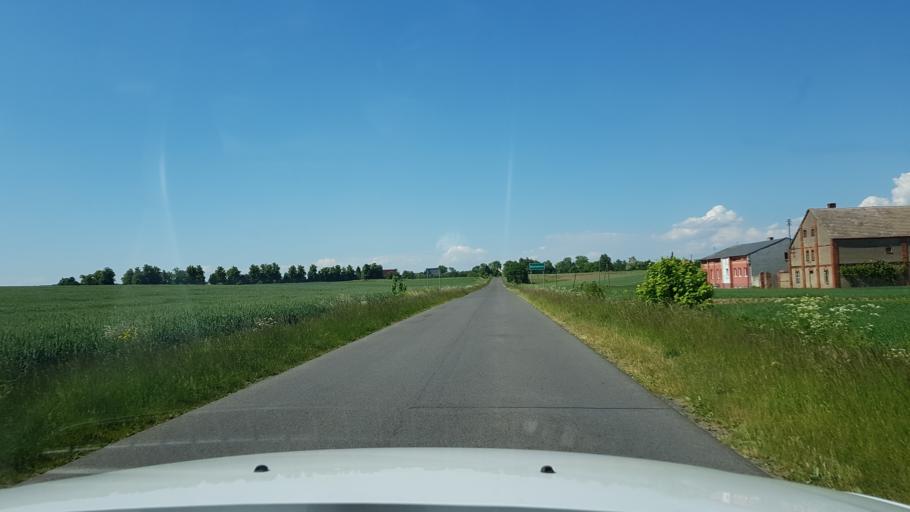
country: PL
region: West Pomeranian Voivodeship
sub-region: Powiat gryfinski
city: Banie
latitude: 53.0745
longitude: 14.6180
